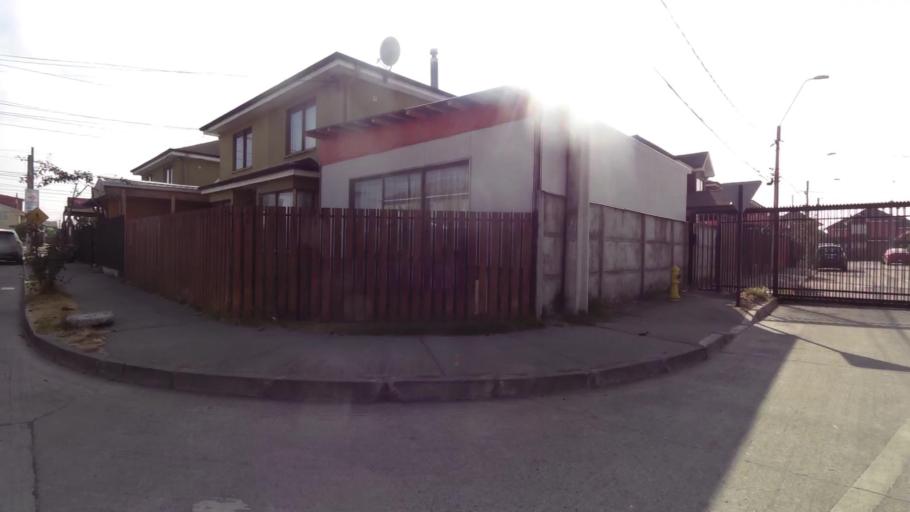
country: CL
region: Biobio
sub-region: Provincia de Concepcion
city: Concepcion
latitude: -36.7992
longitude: -73.1116
